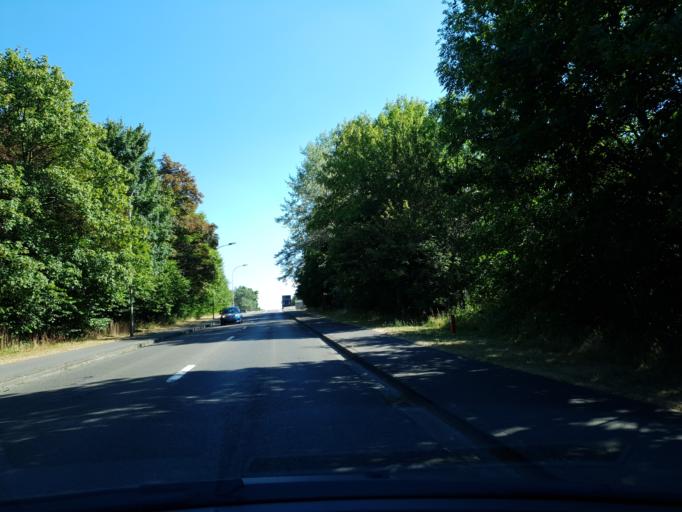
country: BE
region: Flanders
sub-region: Provincie Antwerpen
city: Kapellen
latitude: 51.2691
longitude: 4.4482
